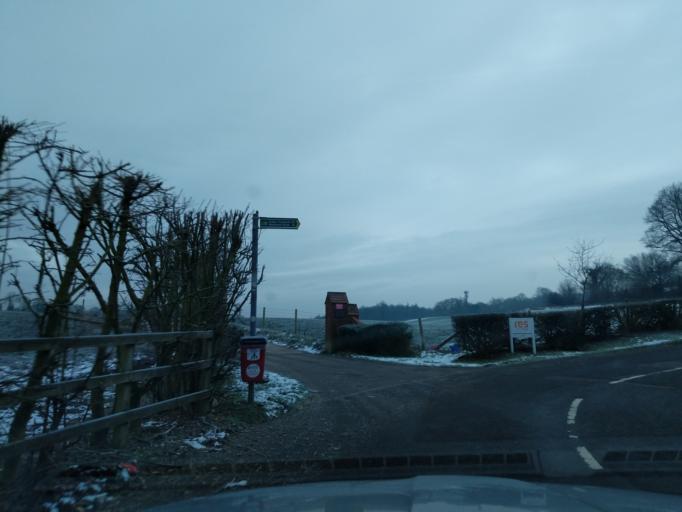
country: GB
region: England
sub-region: Hertfordshire
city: Kings Langley
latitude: 51.7097
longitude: -0.4386
